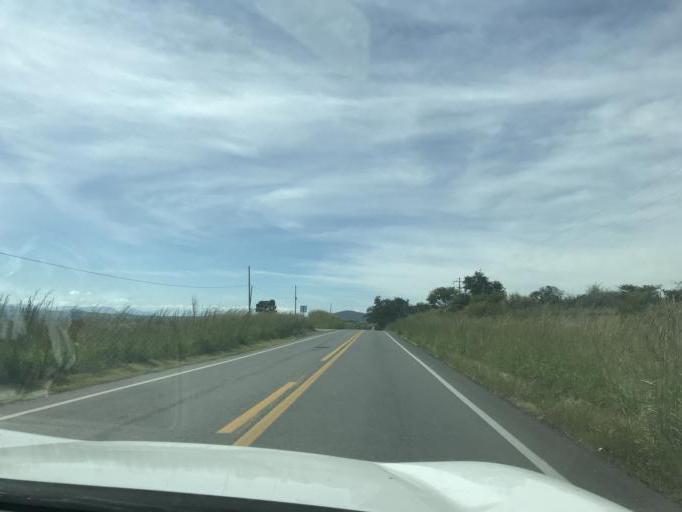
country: MX
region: Guerrero
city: Tepecoacuilco de Trujano
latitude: 18.2803
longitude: -99.5144
